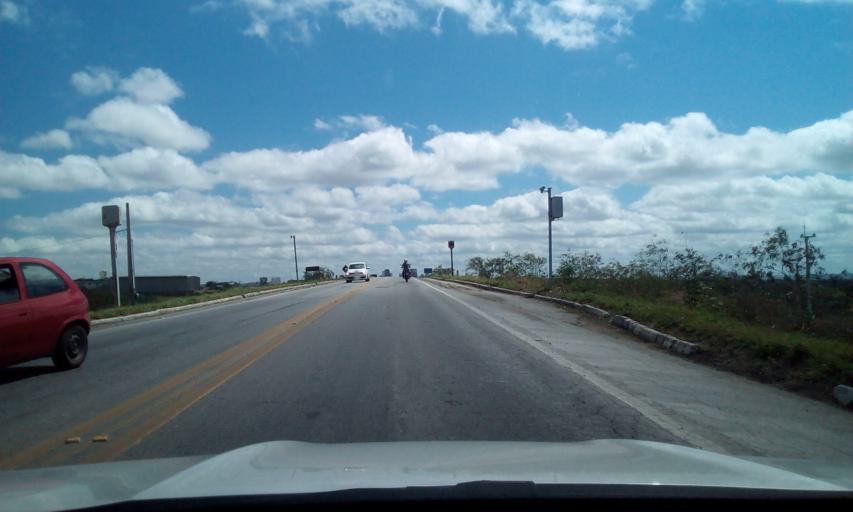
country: BR
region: Paraiba
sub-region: Campina Grande
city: Campina Grande
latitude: -7.2759
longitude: -35.8878
